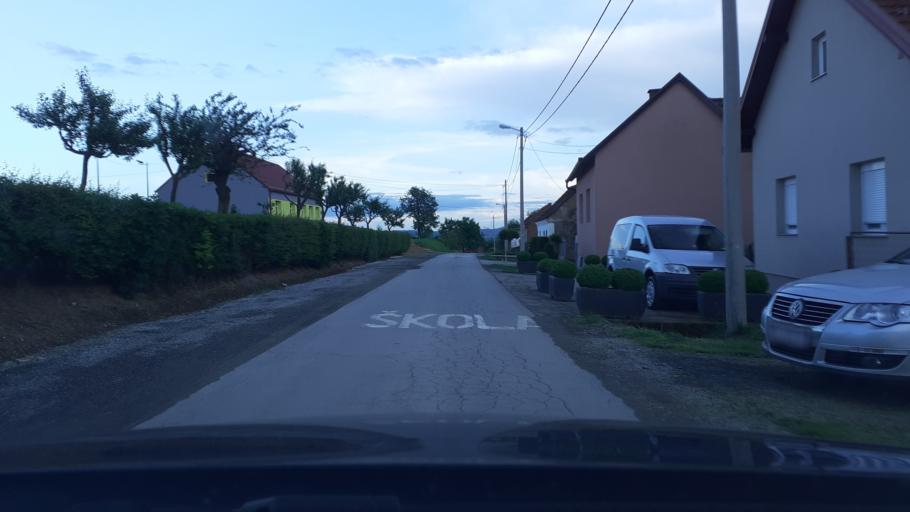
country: HR
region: Pozesko-Slavonska
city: Gradac
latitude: 45.3360
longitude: 17.7962
